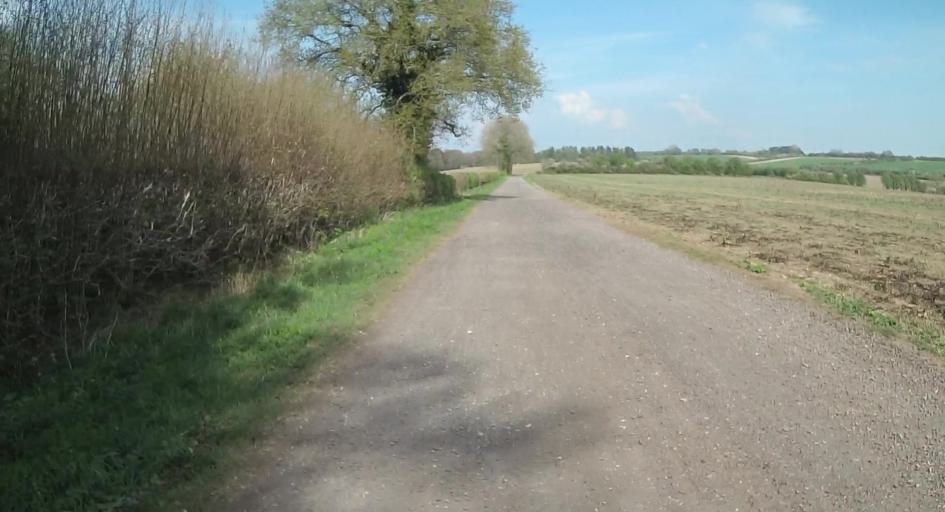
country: GB
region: England
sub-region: Hampshire
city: Basingstoke
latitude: 51.2025
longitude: -1.1562
